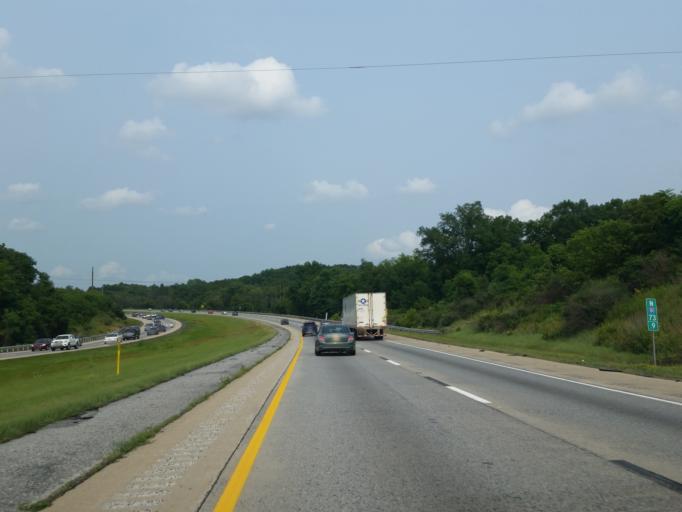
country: US
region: Pennsylvania
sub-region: Dauphin County
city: Linglestown
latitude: 40.3305
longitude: -76.7644
